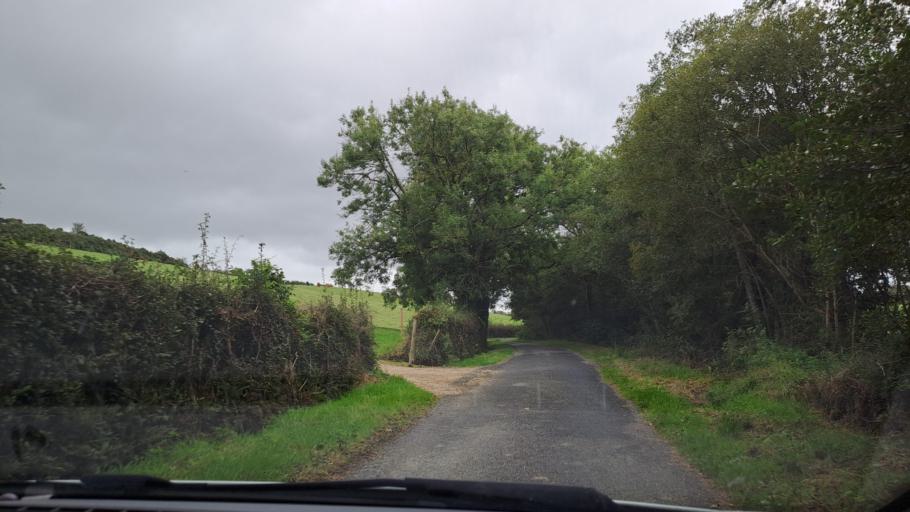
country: IE
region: Ulster
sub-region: An Cabhan
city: Kingscourt
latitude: 53.9725
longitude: -6.8629
